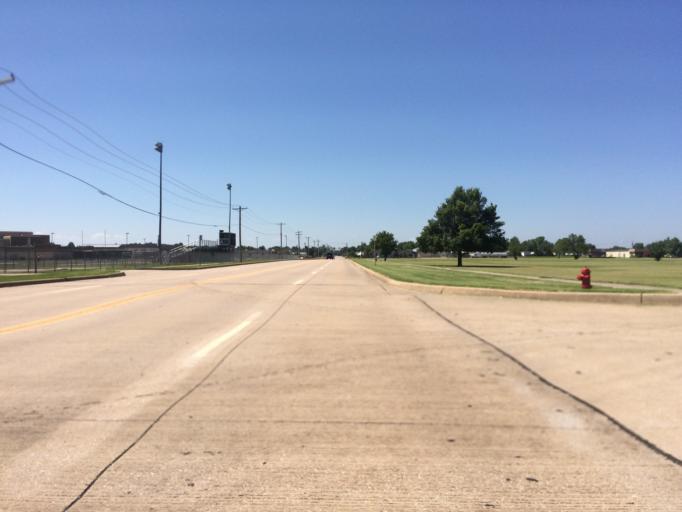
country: US
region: Oklahoma
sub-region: Cleveland County
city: Norman
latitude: 35.2457
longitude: -97.4501
